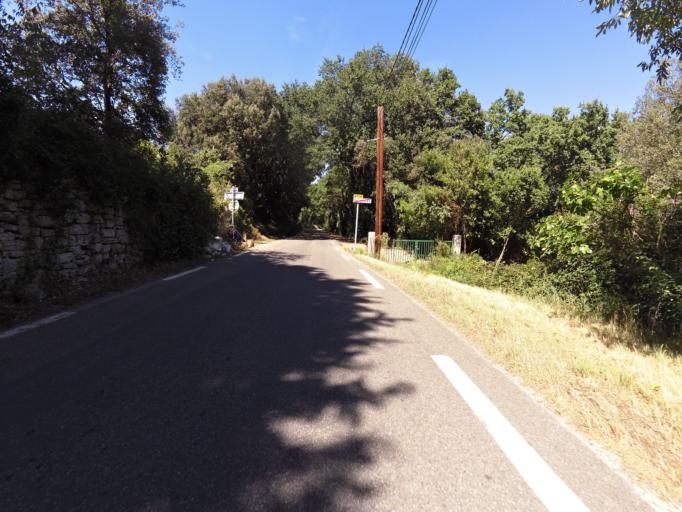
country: FR
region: Languedoc-Roussillon
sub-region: Departement du Gard
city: Sommieres
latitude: 43.8121
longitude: 4.0675
